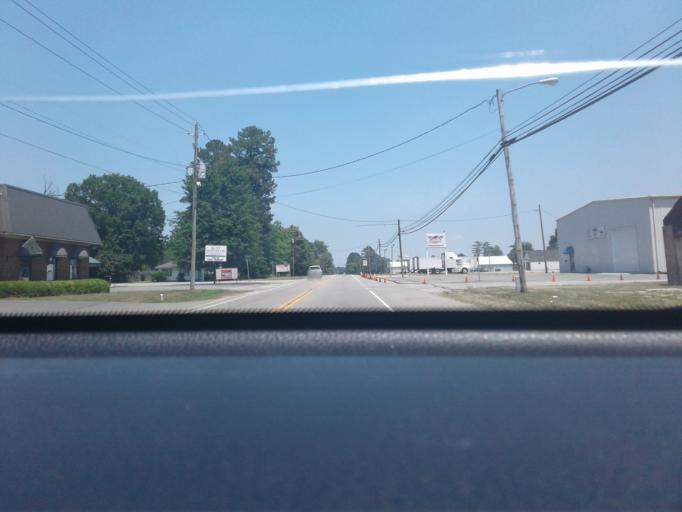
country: US
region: North Carolina
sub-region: Harnett County
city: Dunn
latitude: 35.3208
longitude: -78.6069
